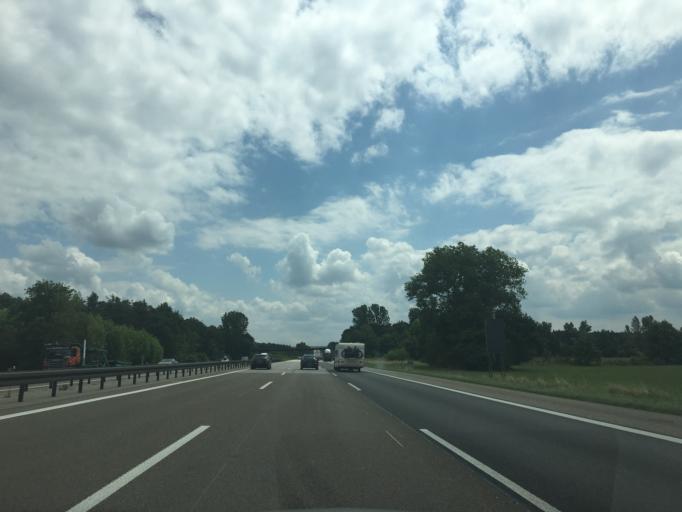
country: DE
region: Bavaria
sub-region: Upper Bavaria
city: Manching
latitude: 48.6862
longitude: 11.4972
